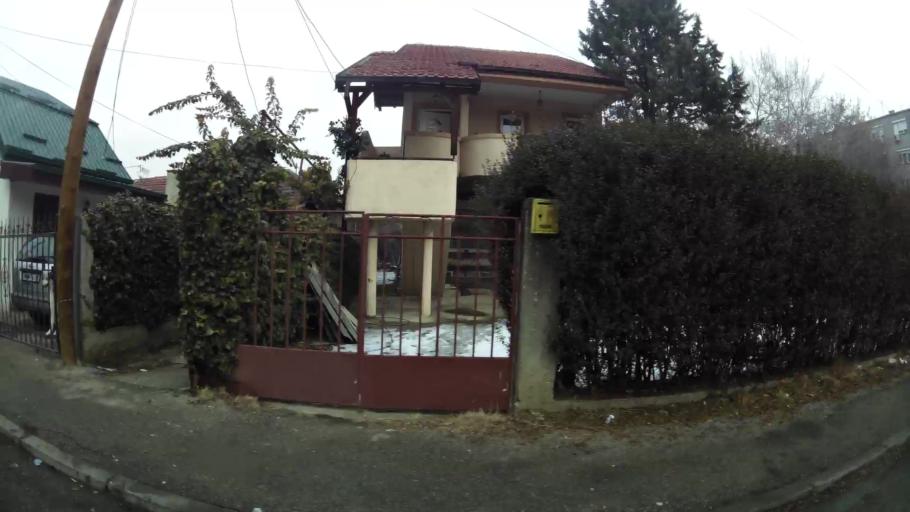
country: MK
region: Kisela Voda
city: Kisela Voda
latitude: 41.9989
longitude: 21.4924
